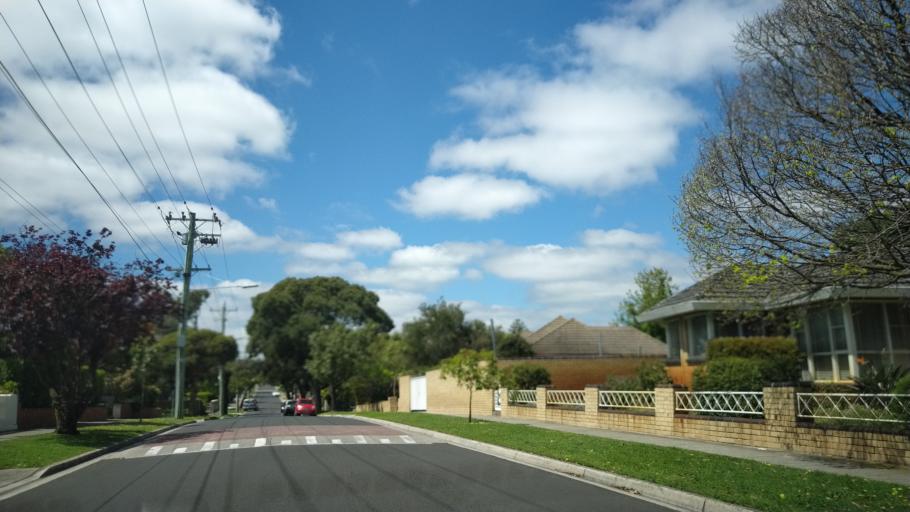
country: AU
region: Victoria
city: Murrumbeena
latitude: -37.9023
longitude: 145.0696
